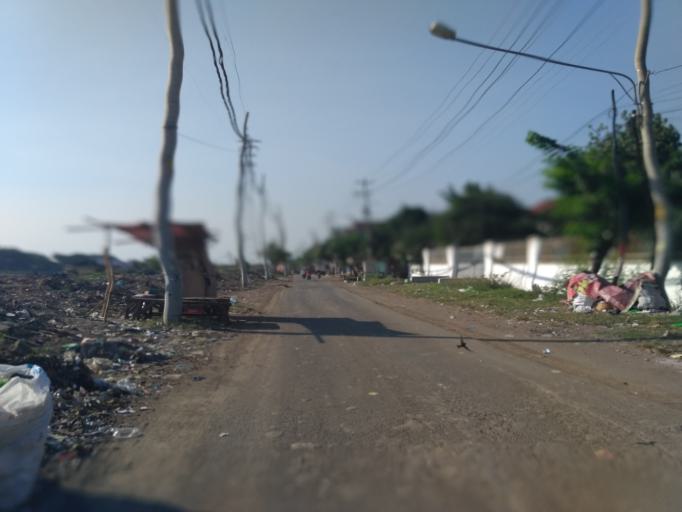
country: ID
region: Central Java
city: Semarang
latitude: -6.9921
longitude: 110.4406
